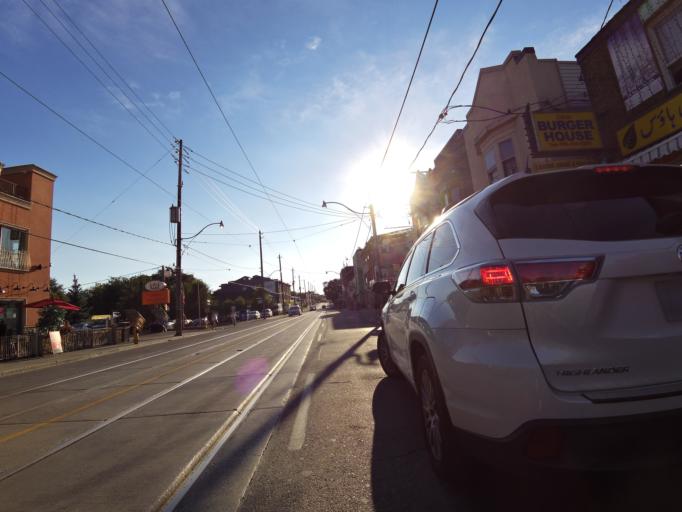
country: CA
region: Ontario
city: Toronto
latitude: 43.6717
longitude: -79.3245
